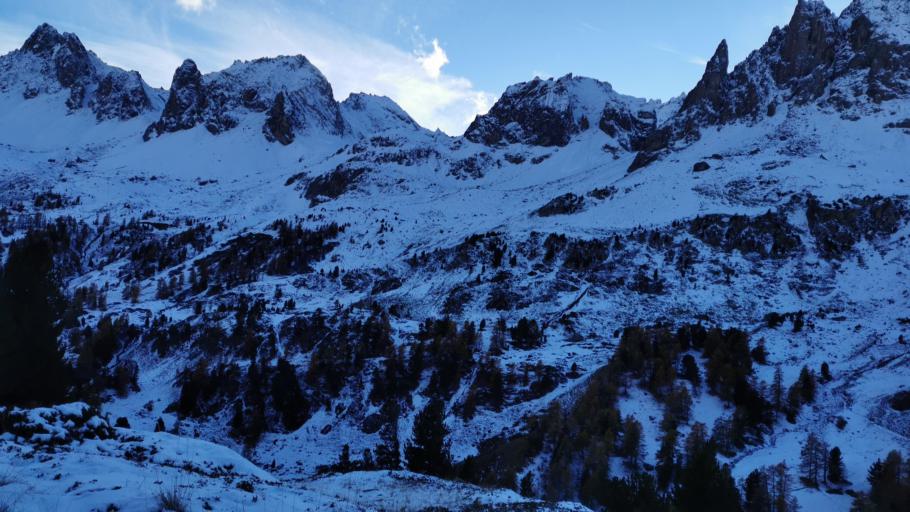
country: FR
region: Provence-Alpes-Cote d'Azur
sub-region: Departement des Hautes-Alpes
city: Le Monetier-les-Bains
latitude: 45.0726
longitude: 6.5163
